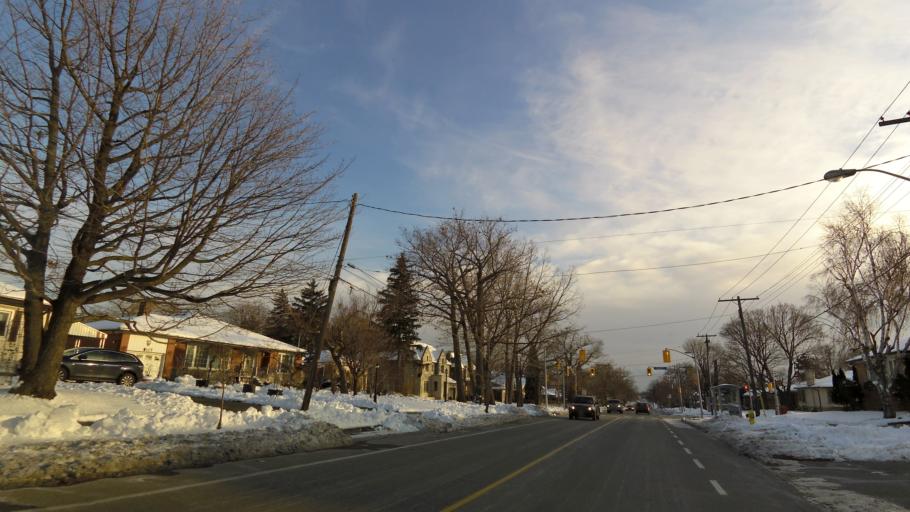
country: CA
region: Ontario
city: Etobicoke
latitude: 43.6698
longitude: -79.5611
